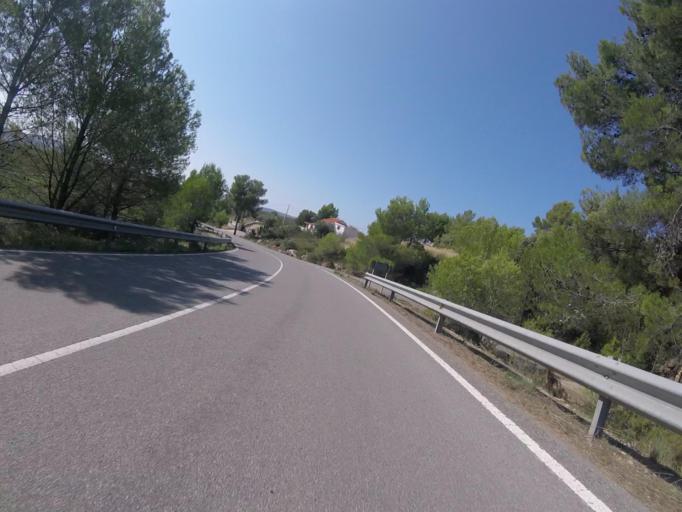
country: ES
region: Valencia
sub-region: Provincia de Castello
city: Adzaneta
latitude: 40.2382
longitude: -0.1891
